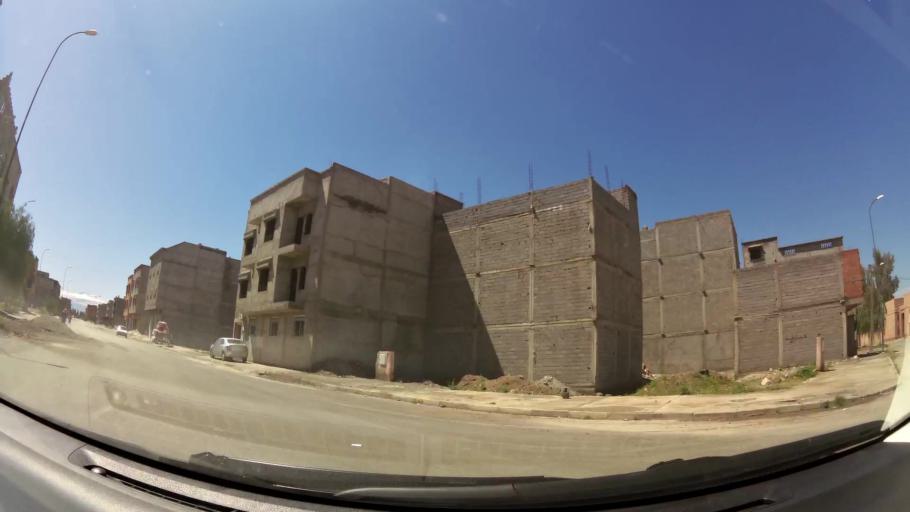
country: MA
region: Marrakech-Tensift-Al Haouz
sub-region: Marrakech
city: Marrakesh
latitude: 31.5548
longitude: -7.9796
